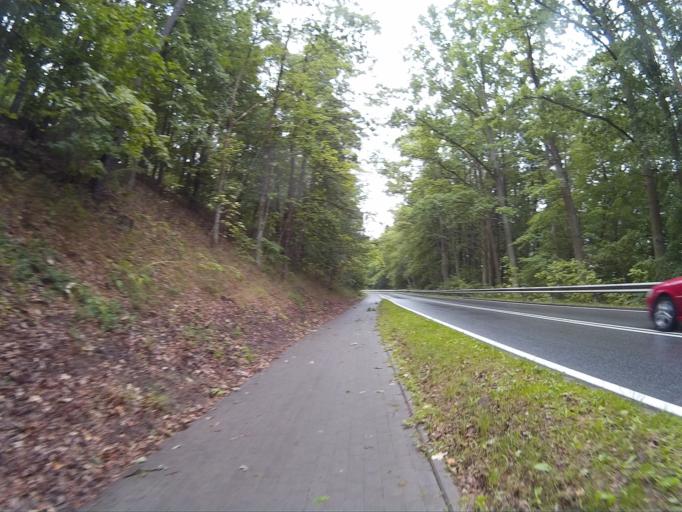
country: PL
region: Kujawsko-Pomorskie
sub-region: Powiat swiecki
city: Osie
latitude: 53.6158
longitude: 18.2758
